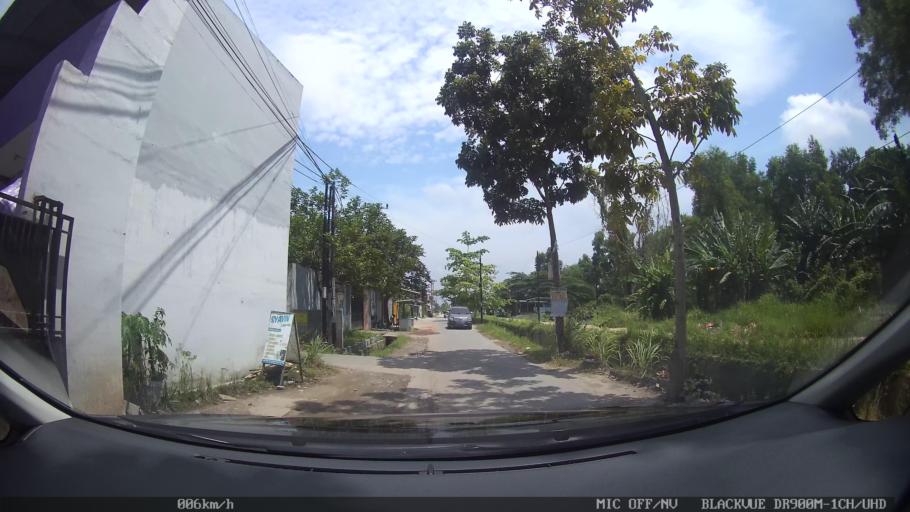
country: ID
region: Lampung
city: Kedaton
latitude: -5.3797
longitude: 105.3009
